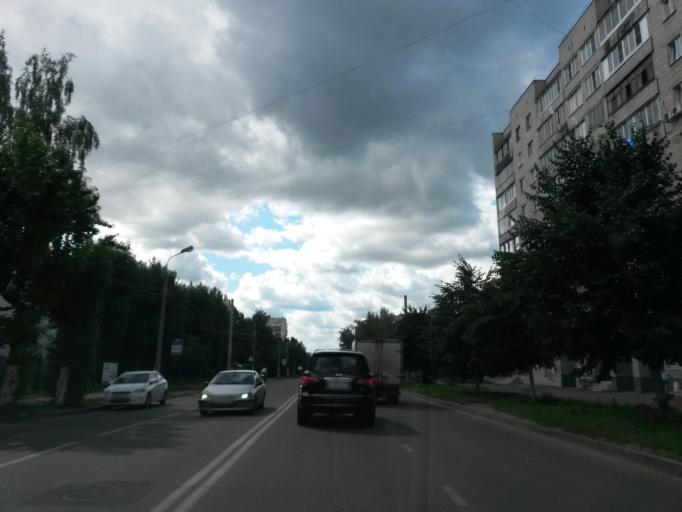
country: RU
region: Jaroslavl
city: Yaroslavl
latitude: 57.6247
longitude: 39.8486
